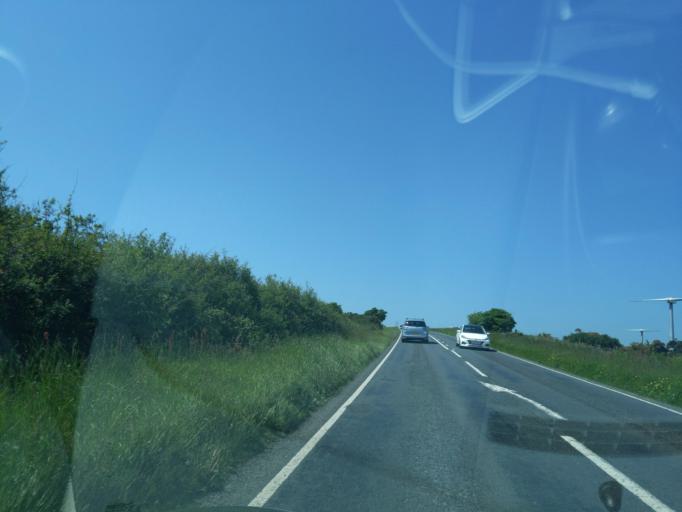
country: GB
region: England
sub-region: Cornwall
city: Trewen
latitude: 50.6420
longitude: -4.5242
